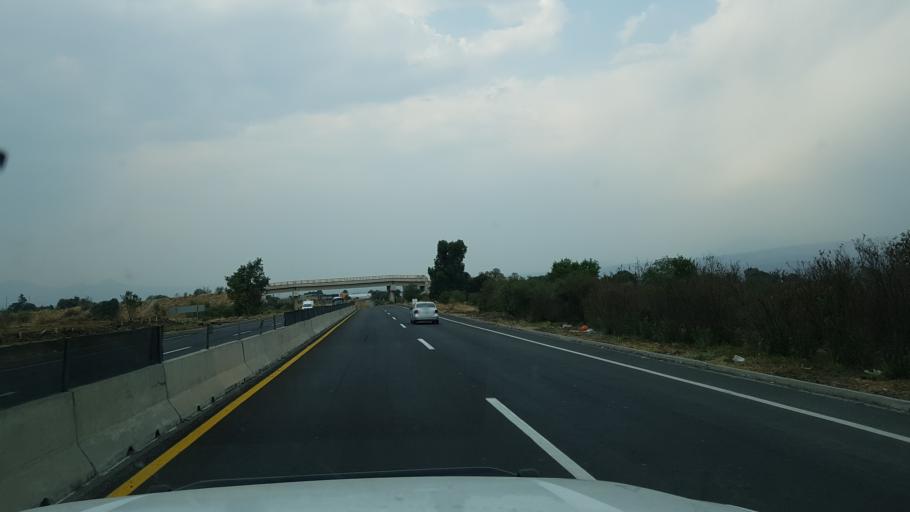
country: MX
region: Mexico
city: Miraflores
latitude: 19.2176
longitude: -98.8302
